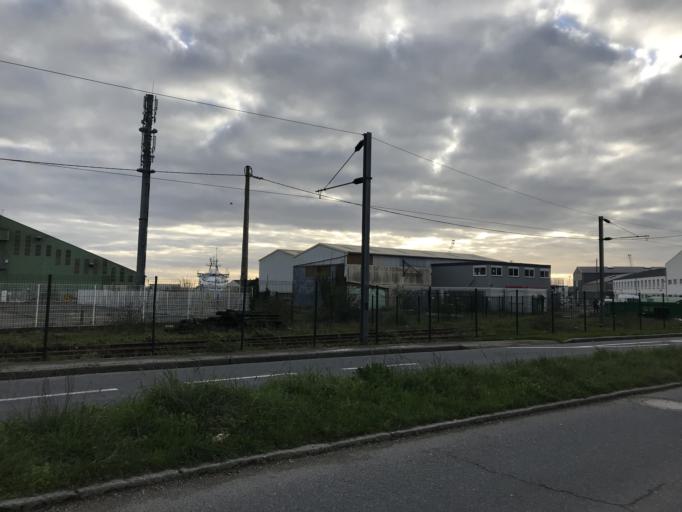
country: FR
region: Brittany
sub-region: Departement du Finistere
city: Brest
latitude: 48.3866
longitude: -4.4716
